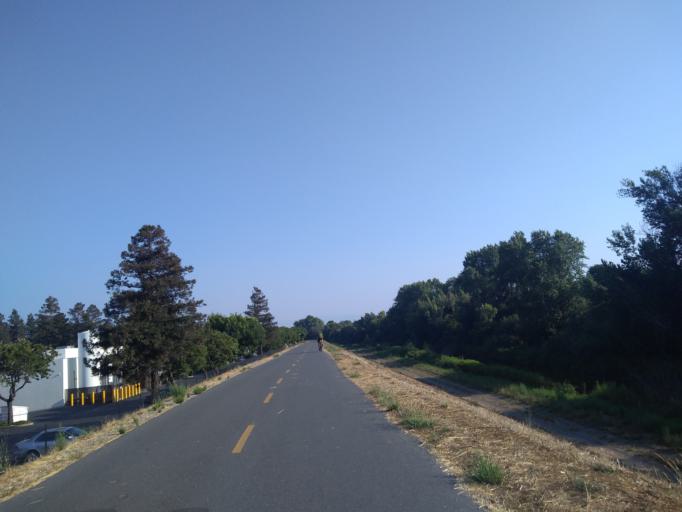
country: US
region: California
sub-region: Santa Clara County
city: Santa Clara
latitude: 37.3934
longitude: -121.9390
